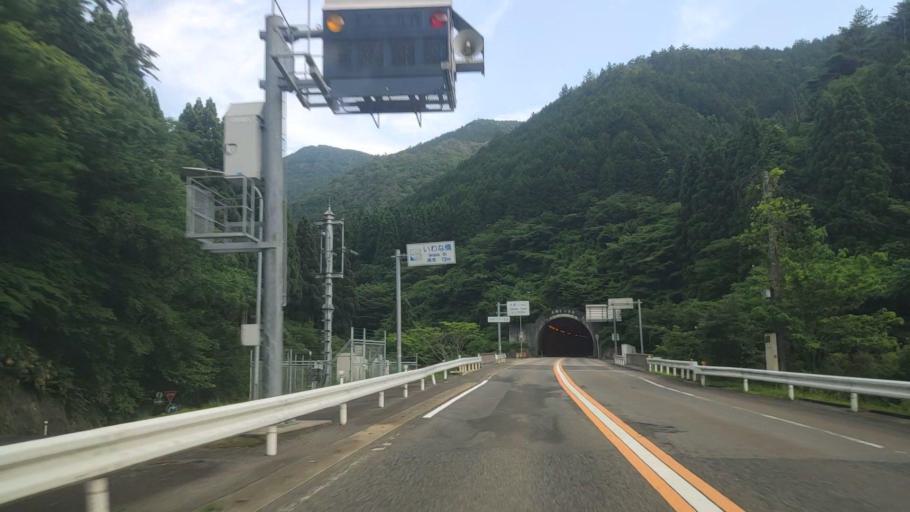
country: JP
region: Tottori
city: Kurayoshi
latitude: 35.3187
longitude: 133.7561
